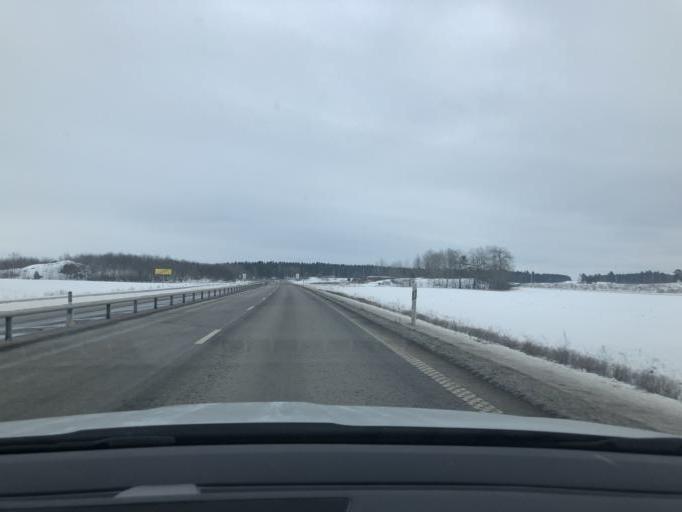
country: SE
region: OEstergoetland
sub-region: Linkopings Kommun
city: Sturefors
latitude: 58.3974
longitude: 15.7112
